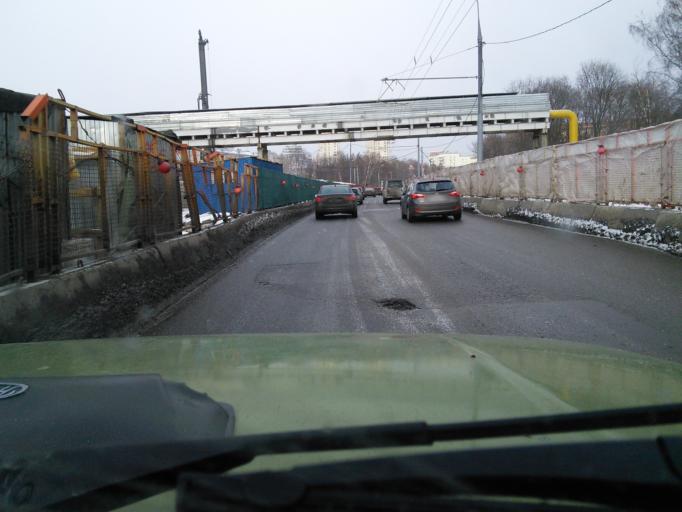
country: RU
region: Moskovskaya
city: Khoroshevo-Mnevniki
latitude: 55.7864
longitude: 37.4830
